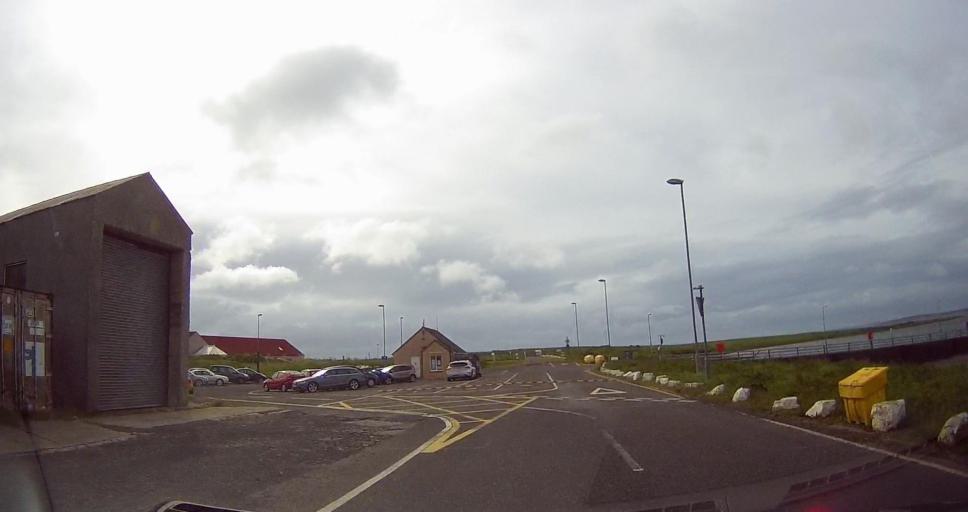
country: GB
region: Scotland
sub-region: Orkney Islands
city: Stromness
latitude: 58.9183
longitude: -3.1843
